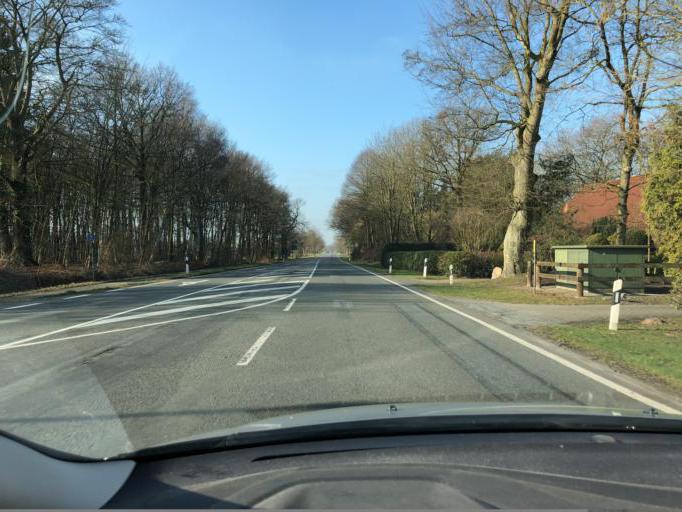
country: DE
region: Lower Saxony
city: Schwerinsdorf
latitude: 53.2975
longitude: 7.7119
